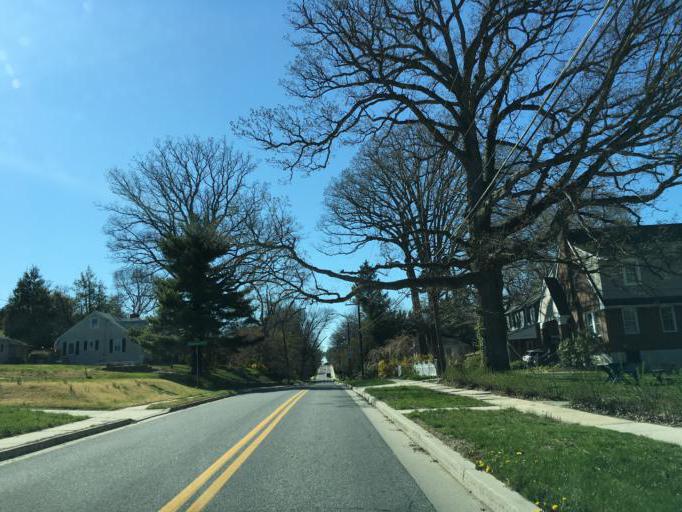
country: US
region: Maryland
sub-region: Baltimore County
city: Towson
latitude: 39.3757
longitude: -76.5904
